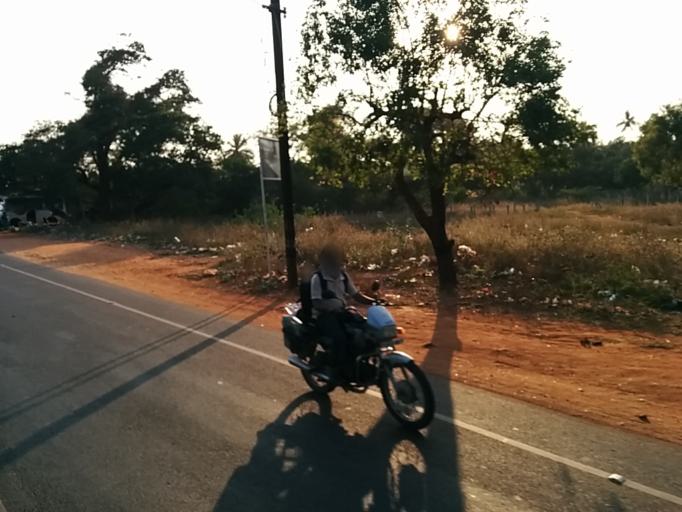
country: IN
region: Tamil Nadu
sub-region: Villupuram
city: Auroville
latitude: 11.9892
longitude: 79.8480
